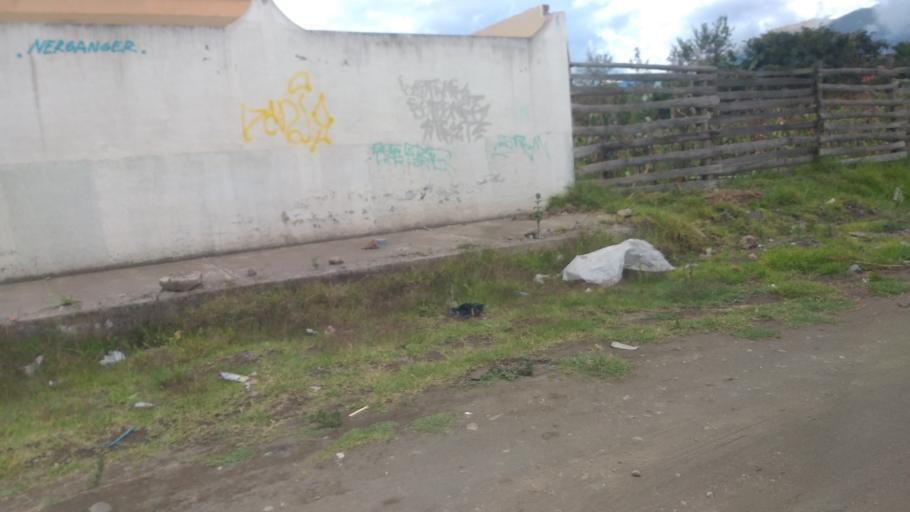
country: EC
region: Chimborazo
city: Riobamba
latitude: -1.6908
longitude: -78.6272
